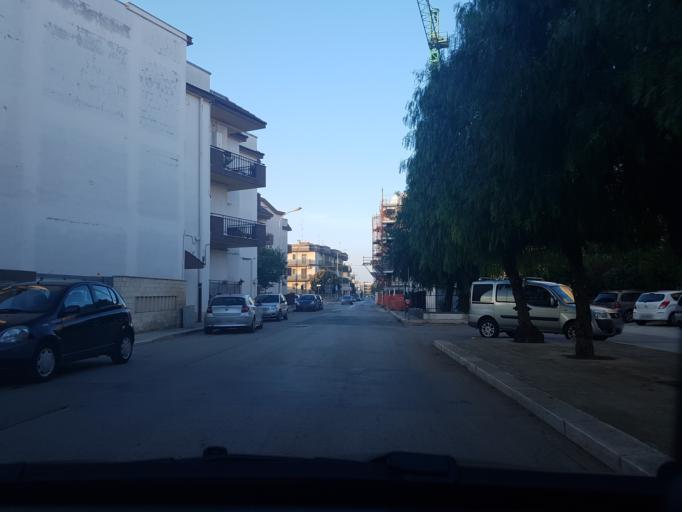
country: IT
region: Apulia
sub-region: Provincia di Bari
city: Bitritto
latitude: 41.0398
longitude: 16.8306
